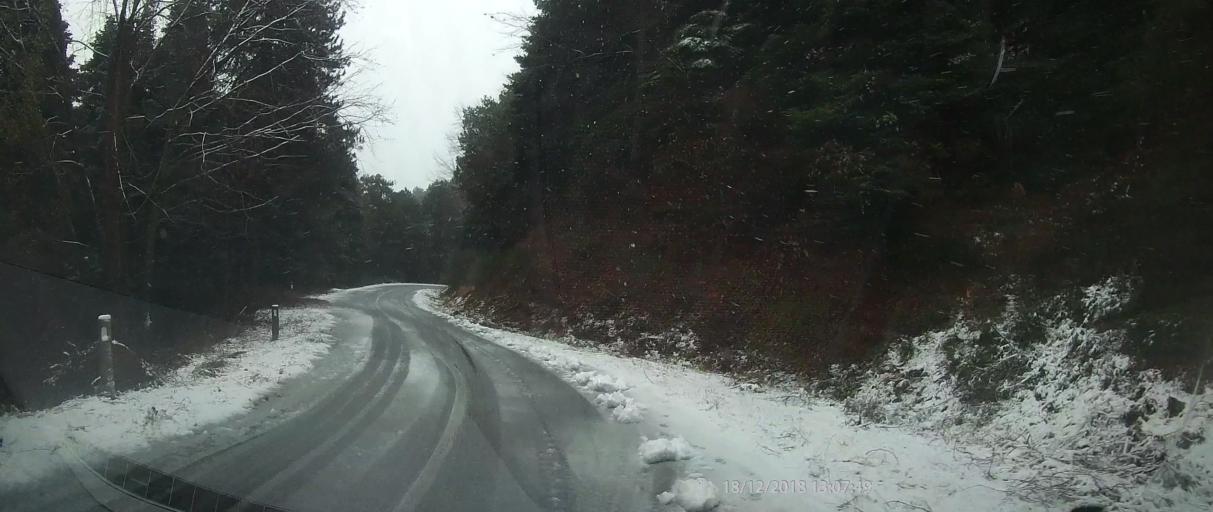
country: GR
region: Central Macedonia
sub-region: Nomos Pierias
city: Litochoro
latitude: 40.1073
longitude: 22.4747
